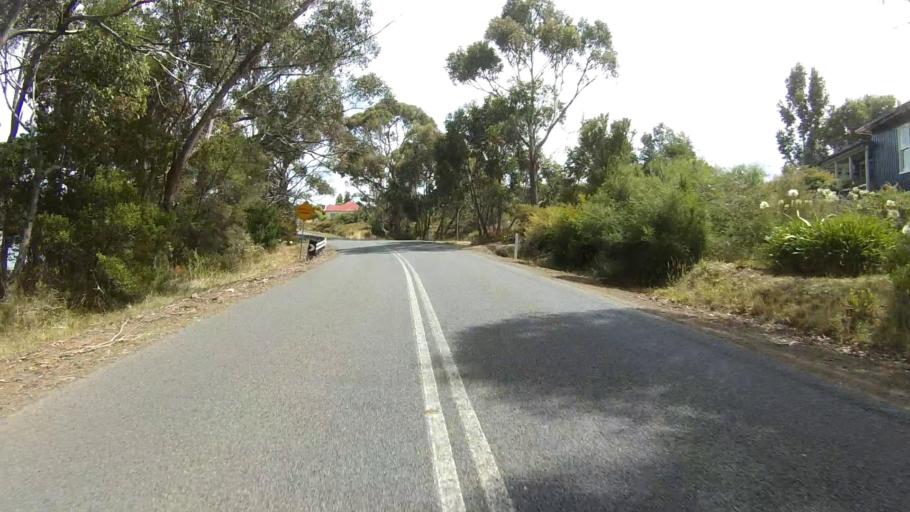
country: AU
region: Tasmania
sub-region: Huon Valley
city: Cygnet
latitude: -43.1909
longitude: 147.1017
